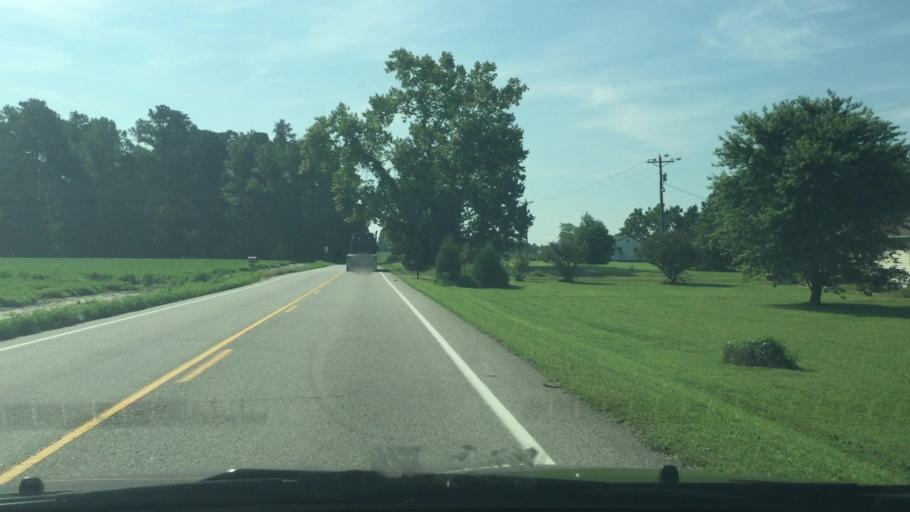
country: US
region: Virginia
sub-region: Sussex County
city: Sussex
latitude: 37.0439
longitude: -77.3123
